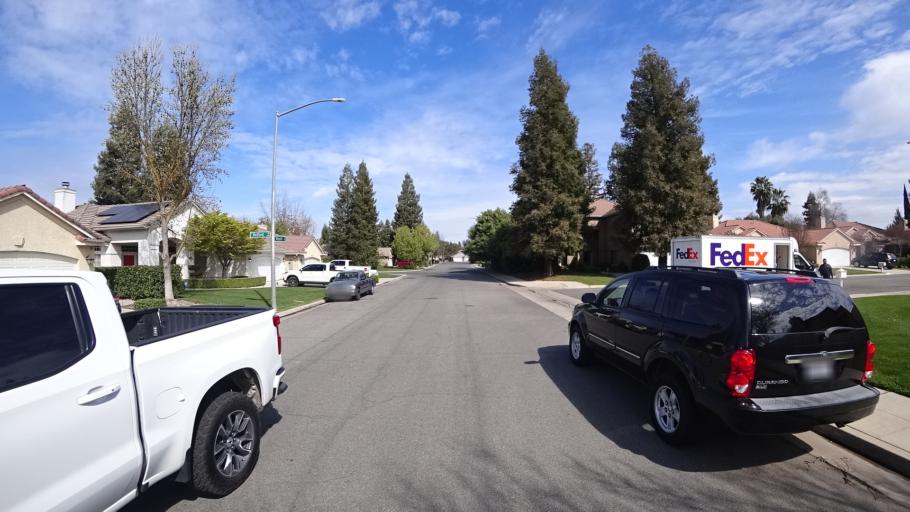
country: US
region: California
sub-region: Fresno County
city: Biola
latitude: 36.8453
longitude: -119.8889
